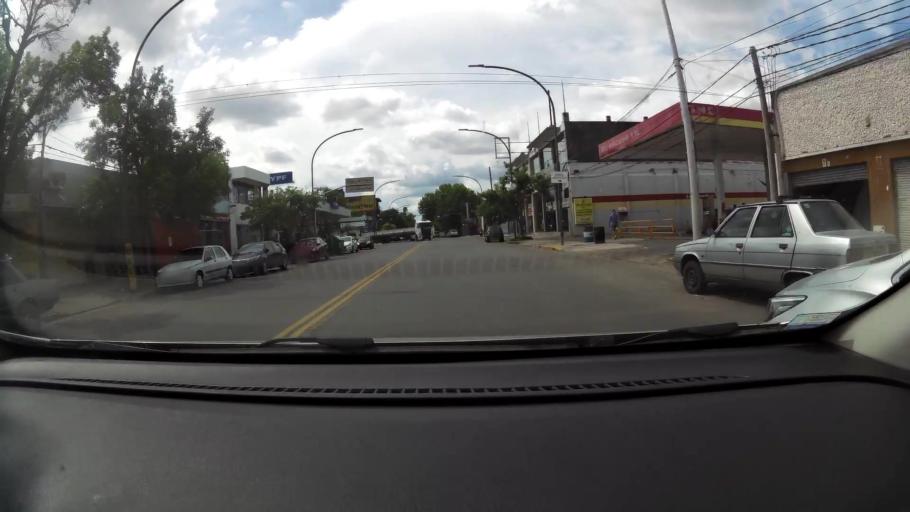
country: AR
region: Santa Fe
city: Gobernador Galvez
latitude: -33.0033
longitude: -60.6360
